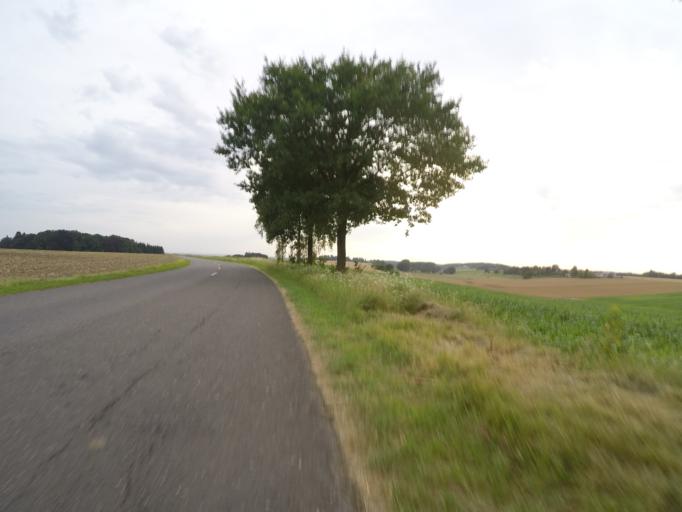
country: BE
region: Wallonia
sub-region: Province de Namur
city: Assesse
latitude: 50.3424
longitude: 5.0095
